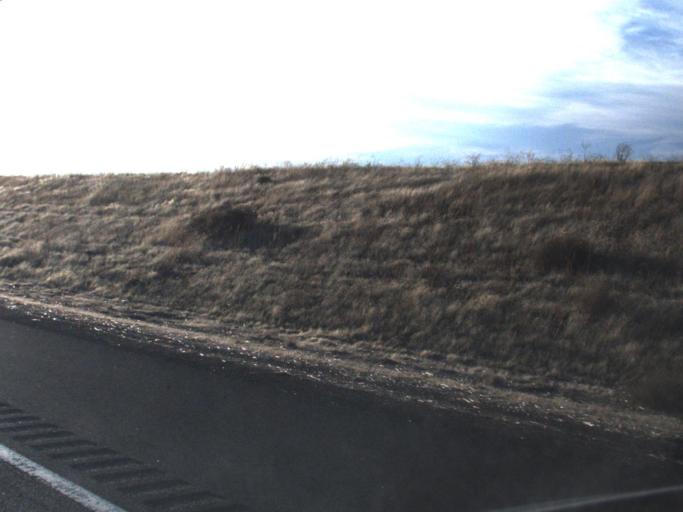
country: US
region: Washington
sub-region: Walla Walla County
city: Garrett
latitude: 46.0648
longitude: -118.4271
